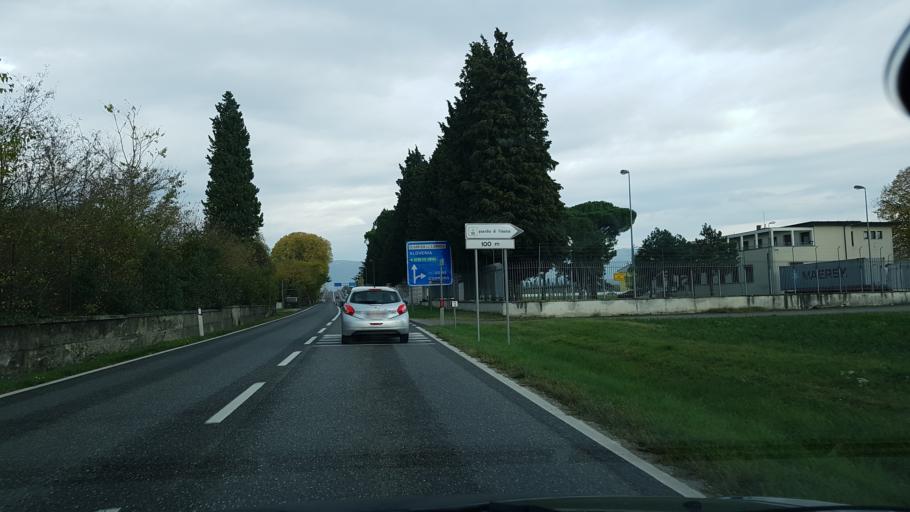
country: SI
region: Miren-Kostanjevica
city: Miren
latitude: 45.9073
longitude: 13.6109
